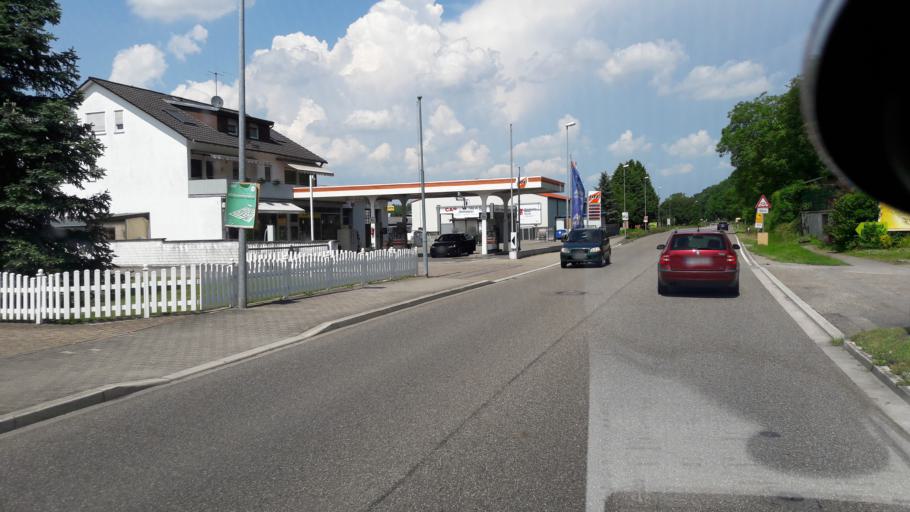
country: DE
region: Baden-Wuerttemberg
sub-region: Karlsruhe Region
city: Weingarten
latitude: 49.0916
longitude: 8.5576
